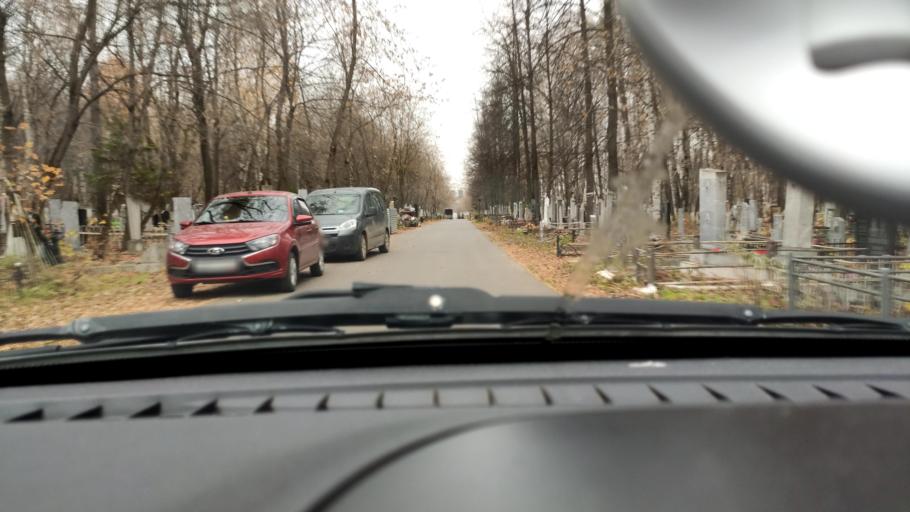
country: RU
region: Perm
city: Perm
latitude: 57.9910
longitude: 56.2841
